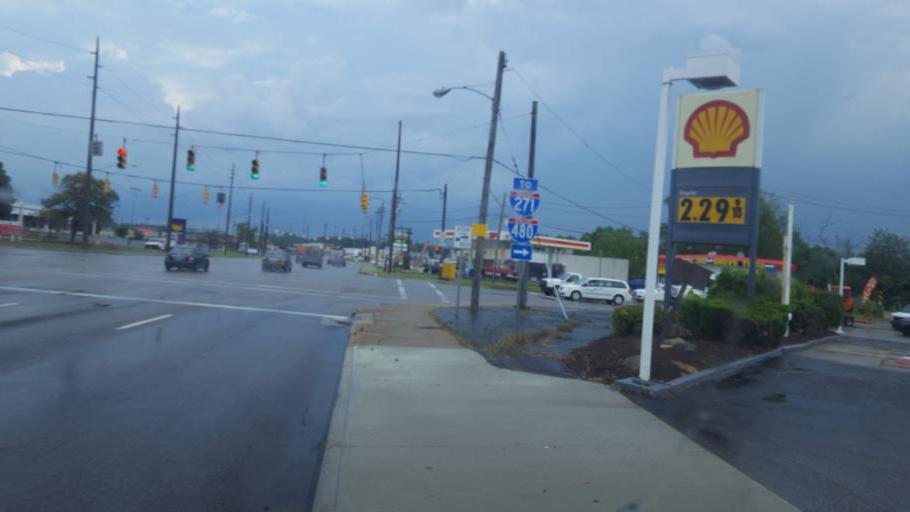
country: US
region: Ohio
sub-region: Cuyahoga County
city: North Randall
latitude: 41.4270
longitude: -81.5260
